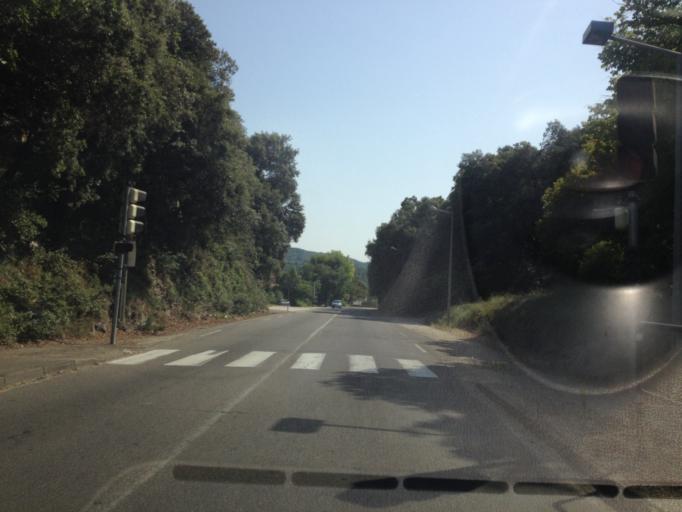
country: FR
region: Provence-Alpes-Cote d'Azur
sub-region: Departement du Vaucluse
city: Vaison-la-Romaine
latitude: 44.2432
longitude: 5.0658
